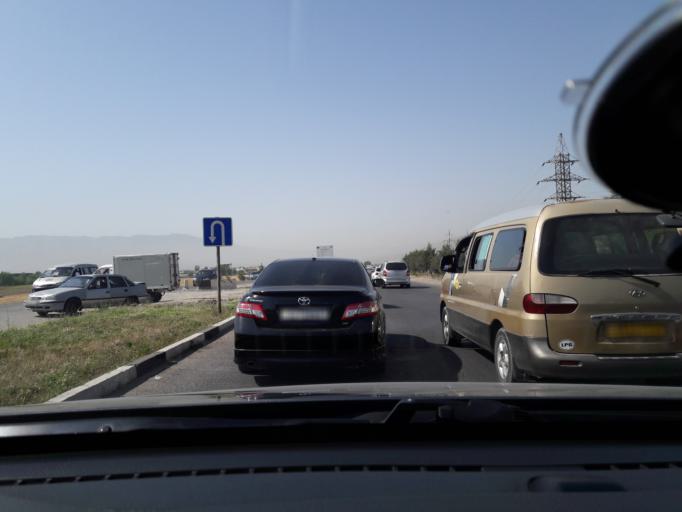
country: TJ
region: Dushanbe
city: Dushanbe
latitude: 38.4986
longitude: 68.7552
